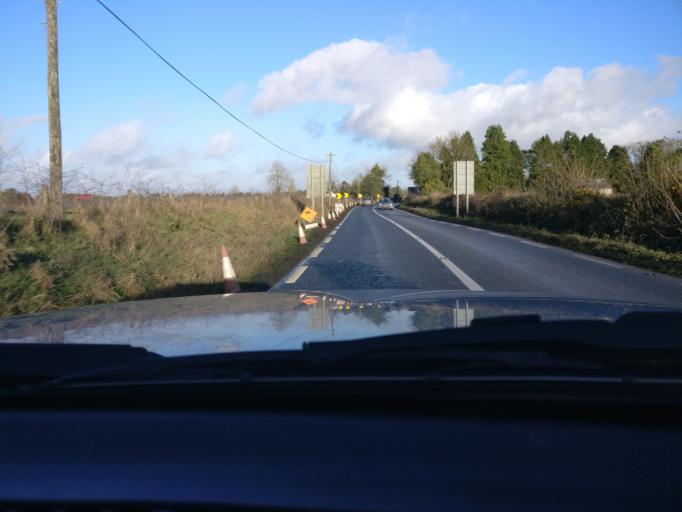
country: IE
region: Leinster
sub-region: An Iarmhi
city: Rathwire
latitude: 53.5763
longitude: -7.1590
